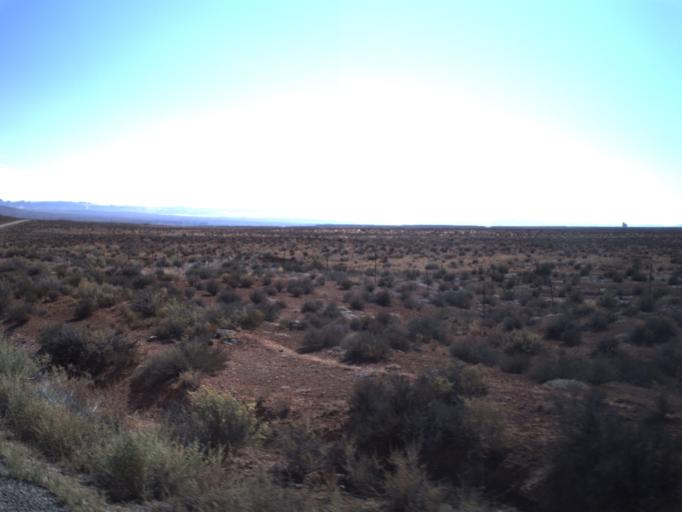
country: US
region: Utah
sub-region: San Juan County
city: Blanding
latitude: 37.2222
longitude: -109.8925
